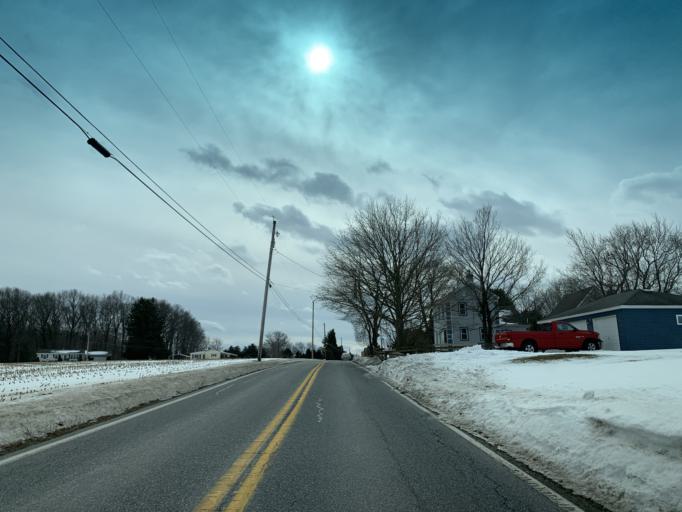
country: US
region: Pennsylvania
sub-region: York County
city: Shrewsbury
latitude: 39.7887
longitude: -76.6369
